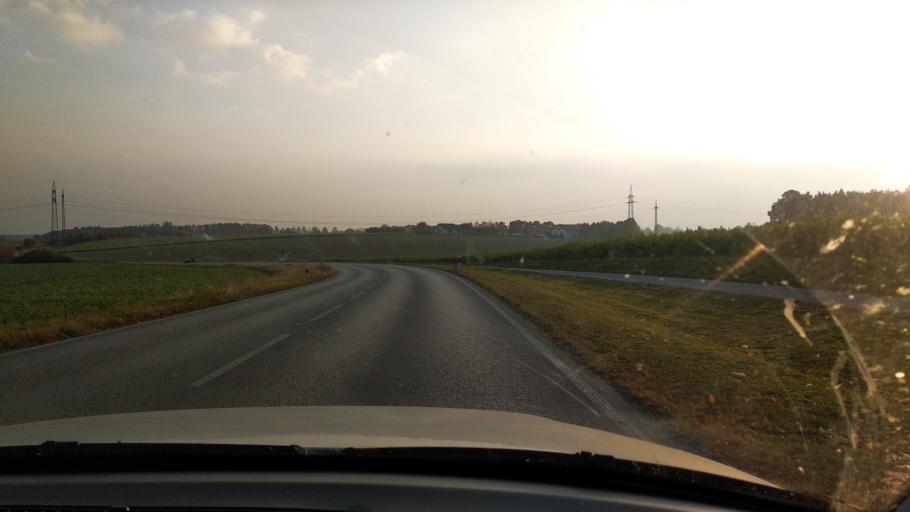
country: DE
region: Bavaria
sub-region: Upper Bavaria
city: Markt Schwaben
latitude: 48.1800
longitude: 11.8649
